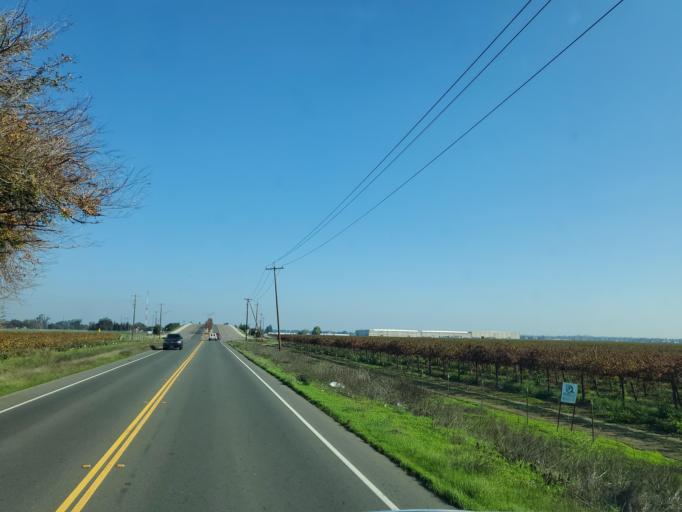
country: US
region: California
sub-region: San Joaquin County
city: Morada
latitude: 38.0574
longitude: -121.2839
